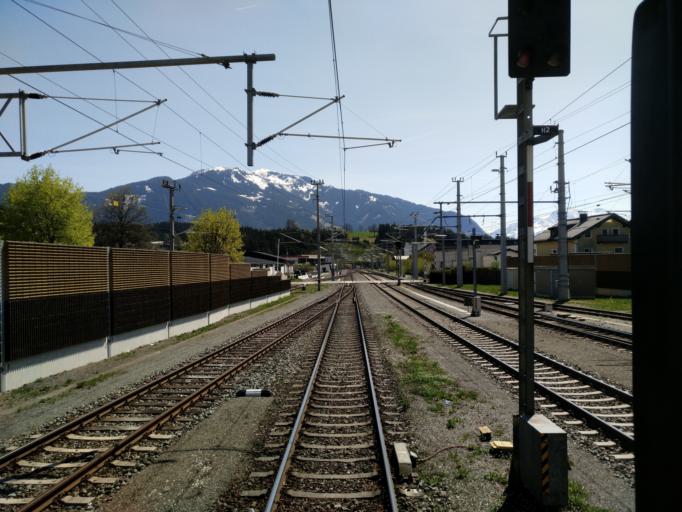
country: AT
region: Salzburg
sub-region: Politischer Bezirk Zell am See
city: Saalfelden am Steinernen Meer
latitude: 47.4248
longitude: 12.8305
